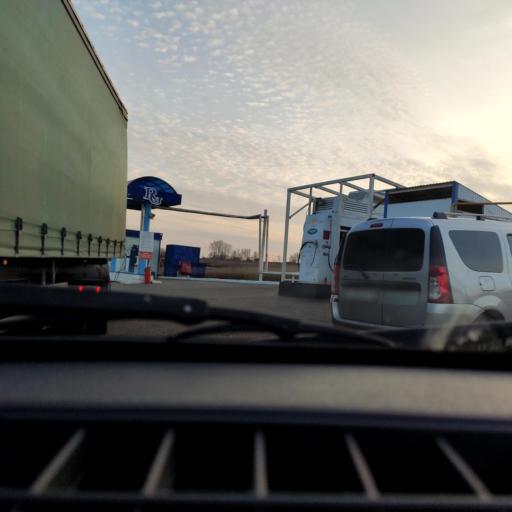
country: RU
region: Bashkortostan
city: Avdon
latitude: 54.7215
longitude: 55.8061
